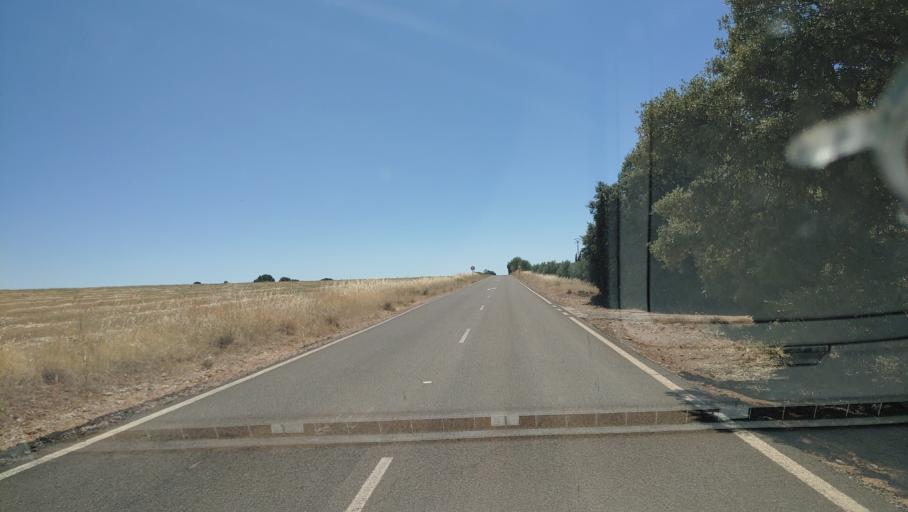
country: ES
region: Castille-La Mancha
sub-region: Provincia de Ciudad Real
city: Villahermosa
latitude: 38.8139
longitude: -2.8339
